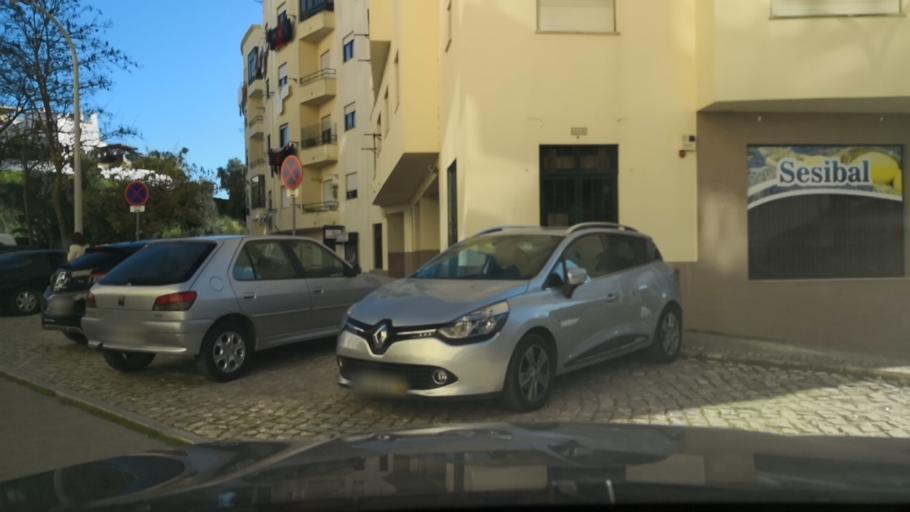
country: PT
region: Setubal
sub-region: Setubal
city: Setubal
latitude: 38.5245
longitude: -8.9055
